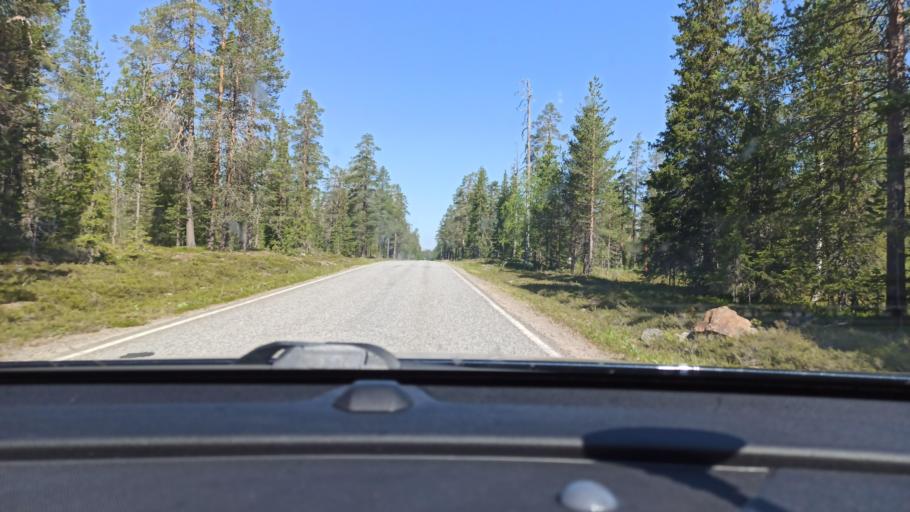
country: FI
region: Lapland
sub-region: Tunturi-Lappi
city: Kolari
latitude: 67.6606
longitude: 24.1654
